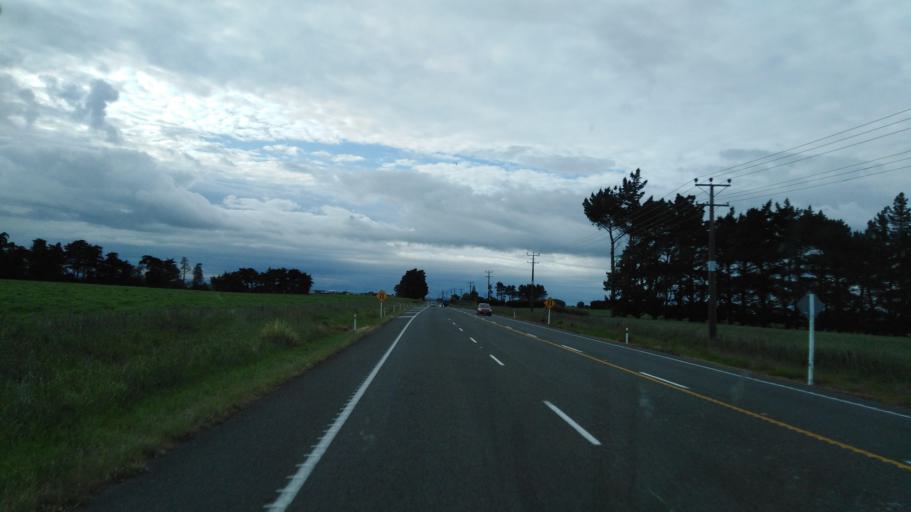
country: NZ
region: Manawatu-Wanganui
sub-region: Rangitikei District
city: Bulls
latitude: -40.1354
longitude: 175.3637
